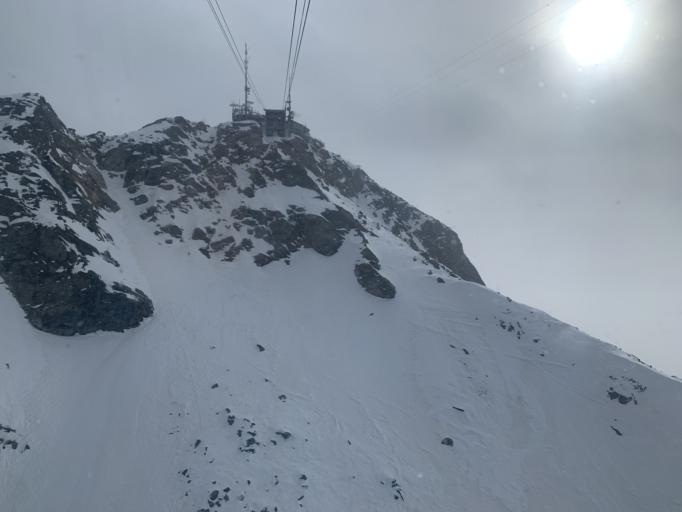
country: CH
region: Grisons
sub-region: Maloja District
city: Silvaplana
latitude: 46.4206
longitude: 9.8219
